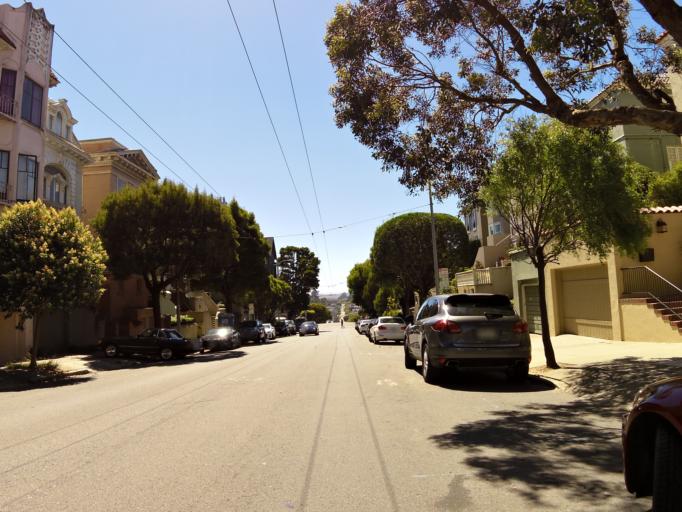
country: US
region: California
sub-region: San Francisco County
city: San Francisco
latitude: 37.7910
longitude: -122.4464
